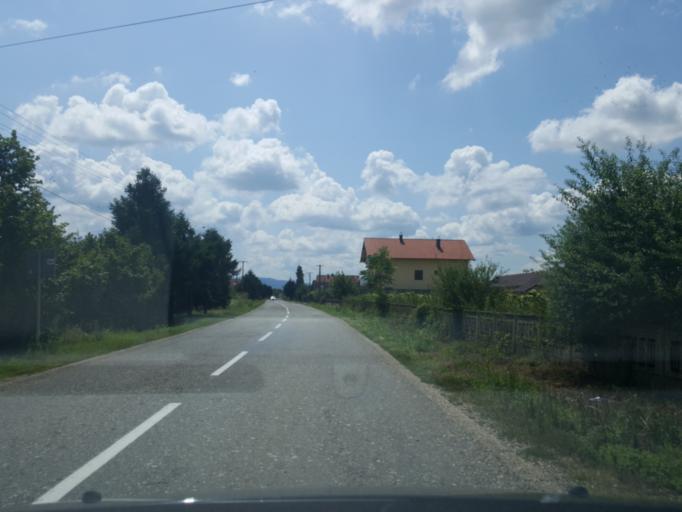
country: RS
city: Zminjak
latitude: 44.7694
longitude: 19.4719
